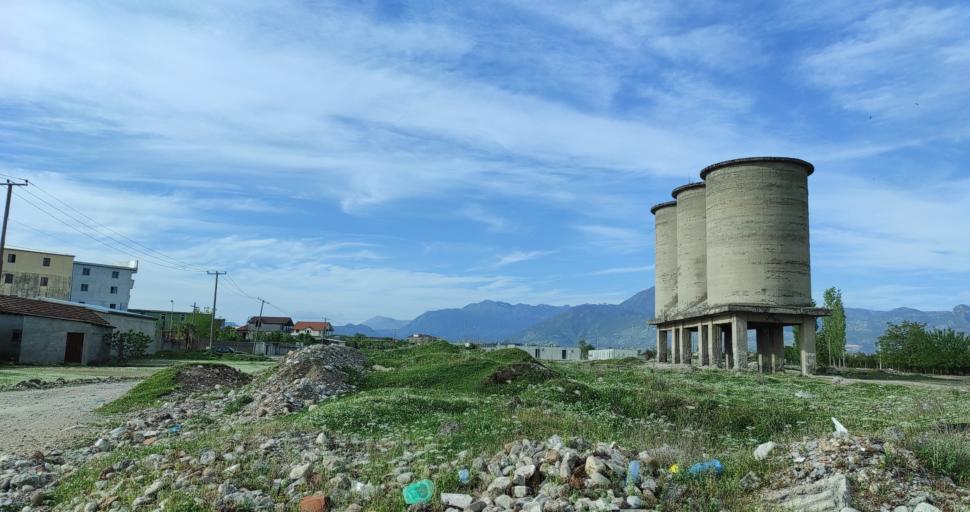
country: AL
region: Shkoder
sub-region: Rrethi i Shkodres
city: Shkoder
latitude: 42.0745
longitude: 19.5298
